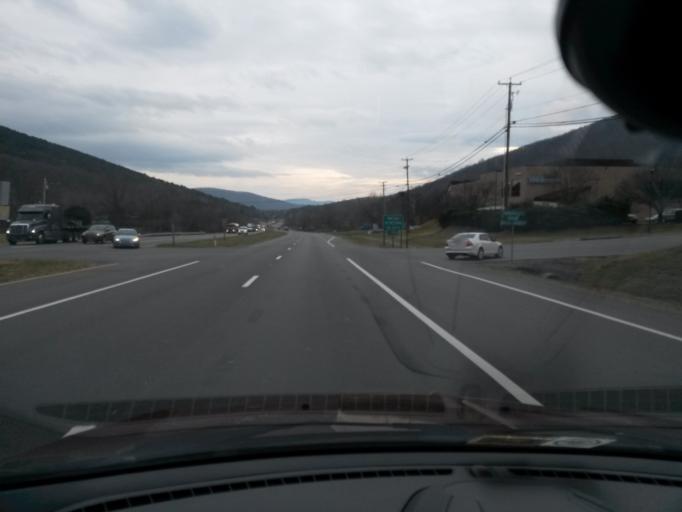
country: US
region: Virginia
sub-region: Botetourt County
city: Cloverdale
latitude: 37.3575
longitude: -79.8852
